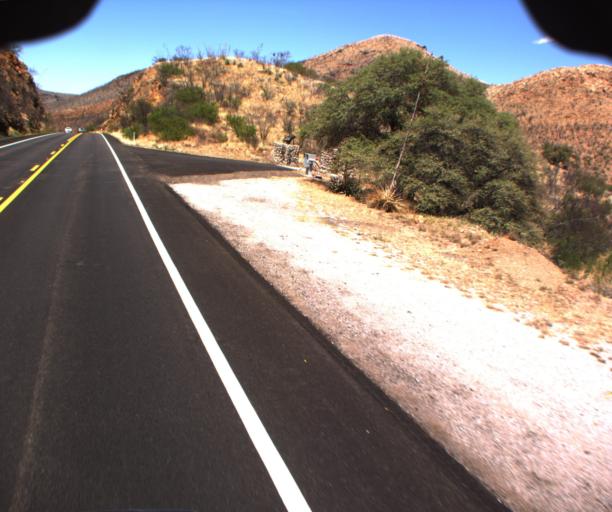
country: US
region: Arizona
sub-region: Cochise County
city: Bisbee
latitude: 31.5036
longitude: -110.0067
